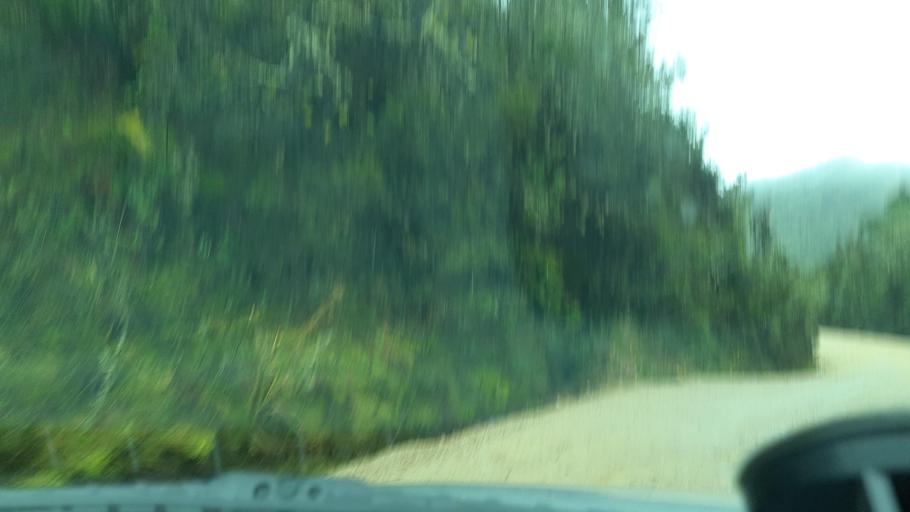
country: CO
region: Cundinamarca
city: Villapinzon
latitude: 5.2115
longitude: -73.5444
